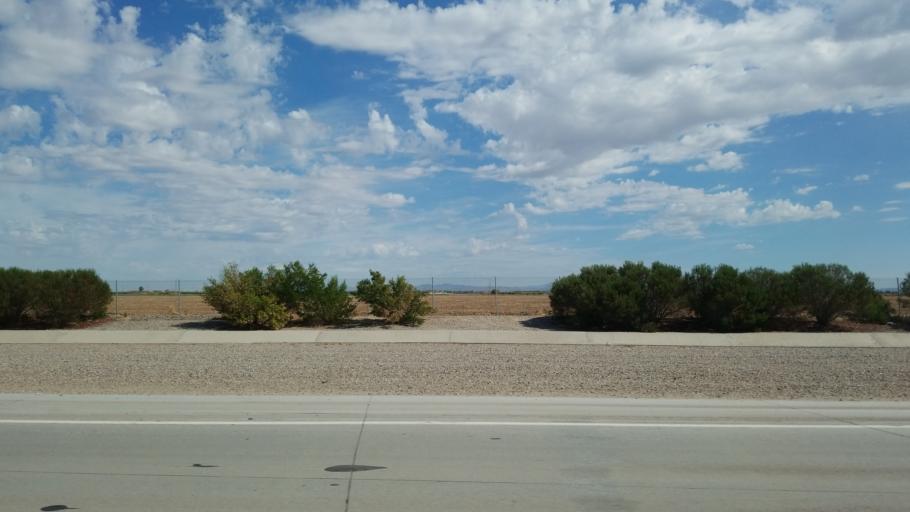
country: US
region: Arizona
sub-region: Maricopa County
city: Citrus Park
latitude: 33.5593
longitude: -112.3974
